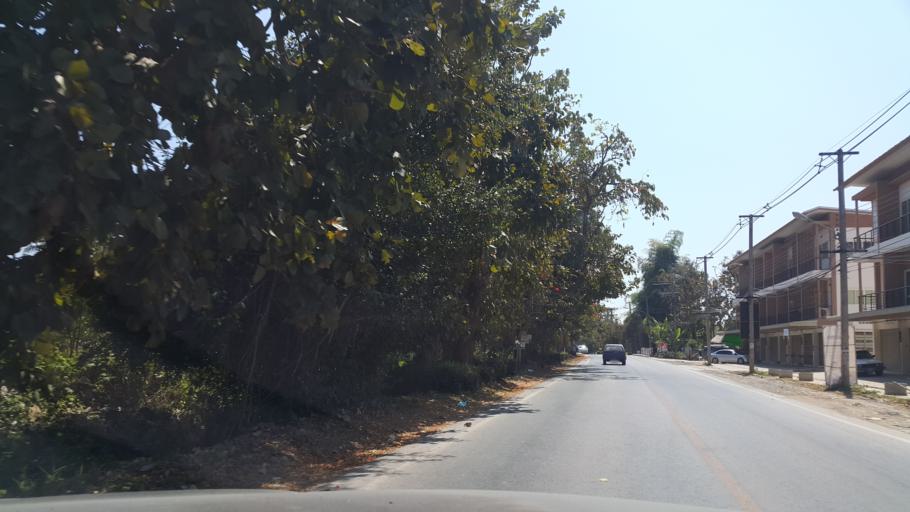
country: TH
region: Chiang Mai
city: San Sai
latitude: 18.8633
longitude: 99.0524
